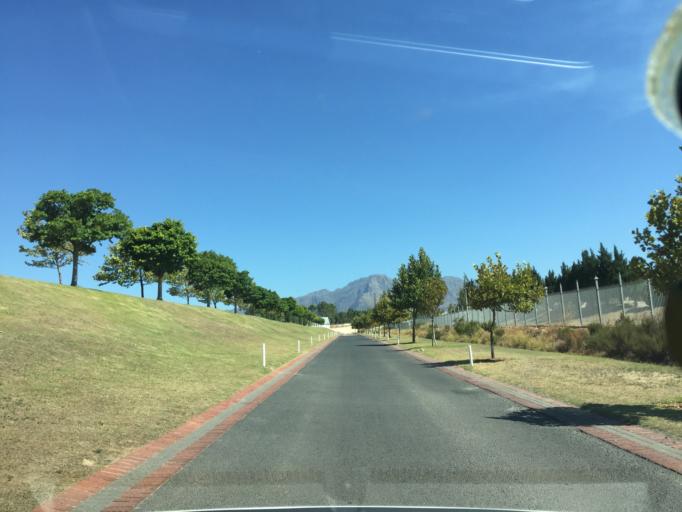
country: ZA
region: Western Cape
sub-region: Cape Winelands District Municipality
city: Paarl
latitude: -33.8060
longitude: 18.9733
